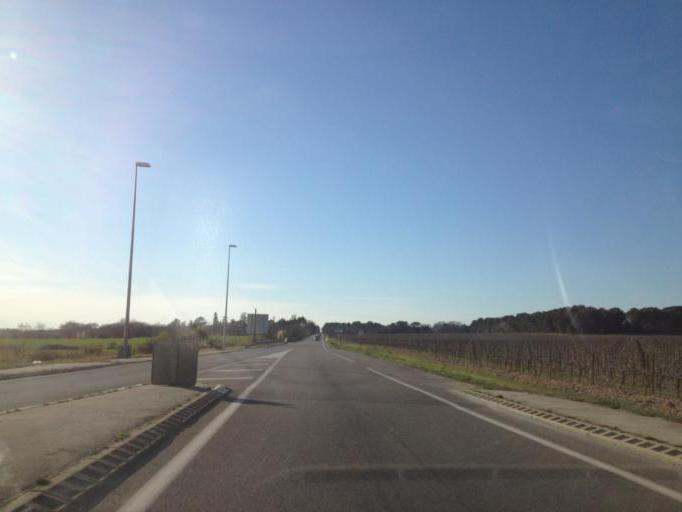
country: FR
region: Provence-Alpes-Cote d'Azur
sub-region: Departement des Bouches-du-Rhone
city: Eguilles
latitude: 43.5868
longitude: 5.3686
